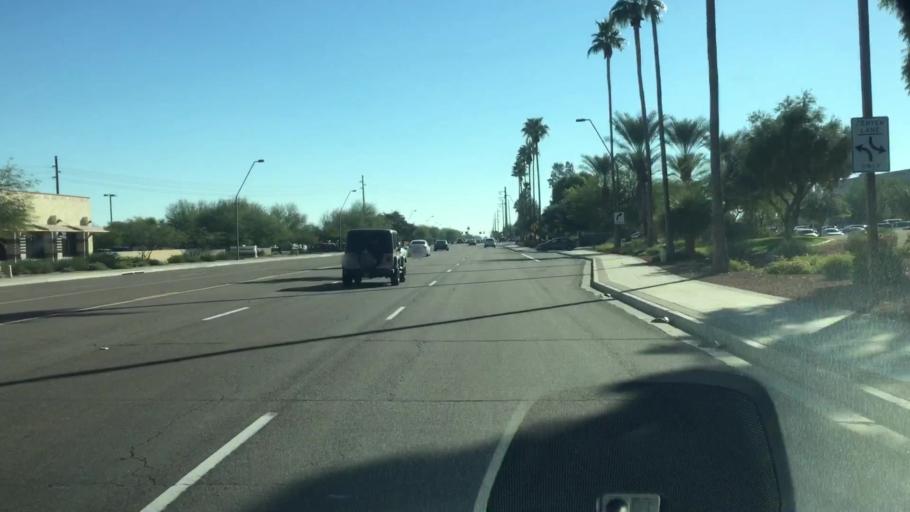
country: US
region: Arizona
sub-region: Maricopa County
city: Guadalupe
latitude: 33.3393
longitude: -111.9632
